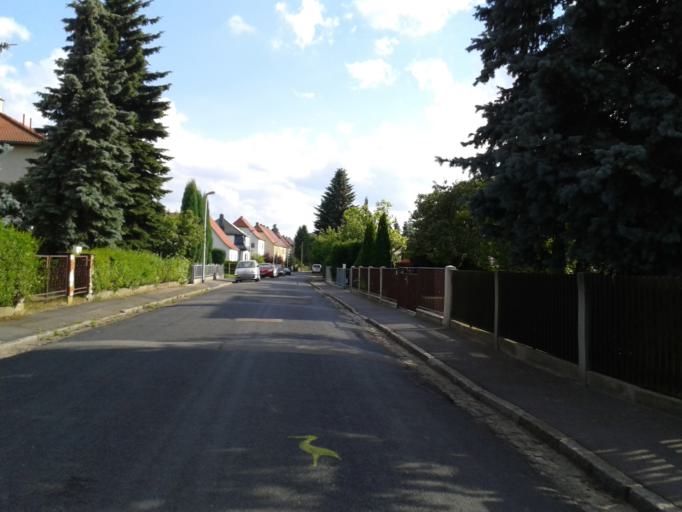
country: DE
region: Saxony
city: Albertstadt
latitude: 51.1137
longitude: 13.7411
